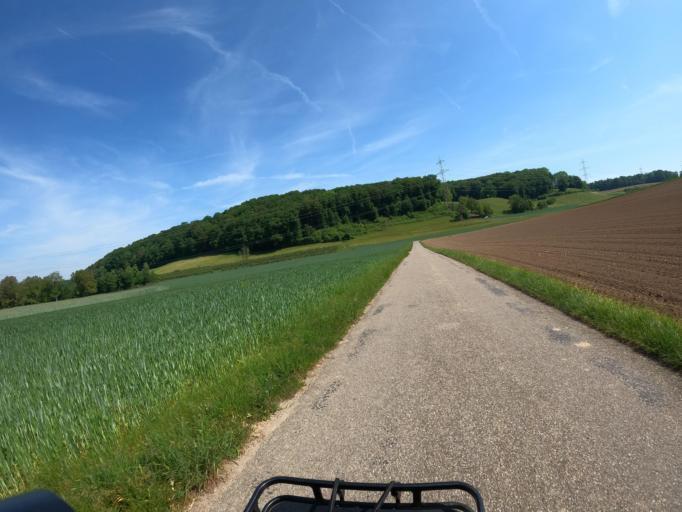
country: CH
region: Zurich
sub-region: Bezirk Buelach
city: Buelach / Gstueckt
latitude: 47.5309
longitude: 8.5497
